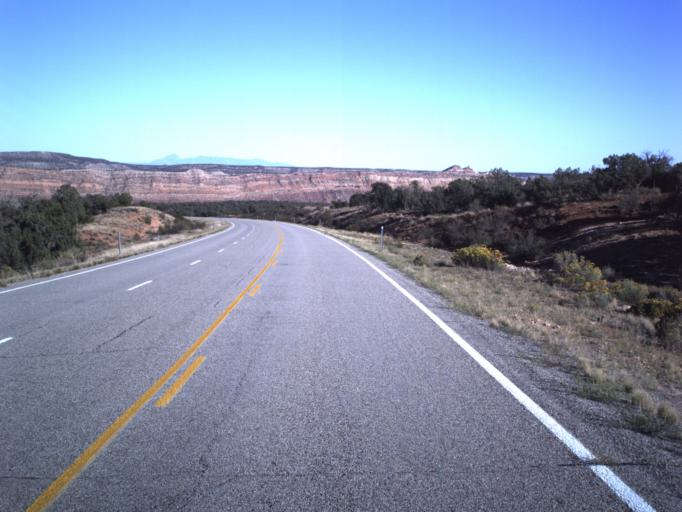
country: US
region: Utah
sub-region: San Juan County
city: Blanding
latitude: 37.5299
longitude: -109.6954
